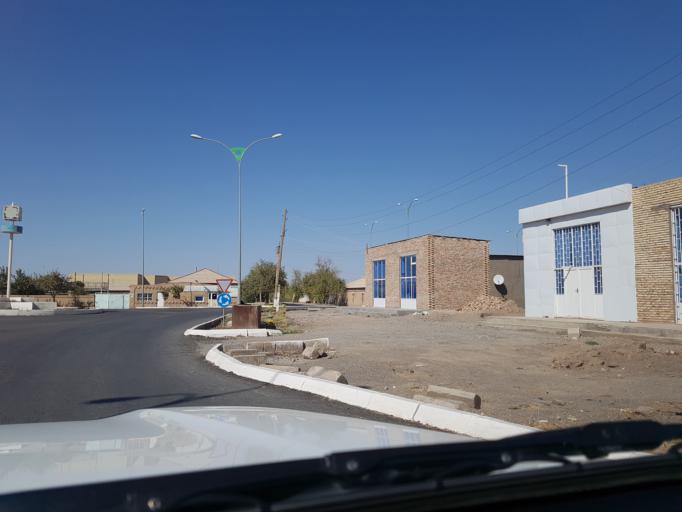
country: IR
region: Razavi Khorasan
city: Sarakhs
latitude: 36.5231
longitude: 61.2171
